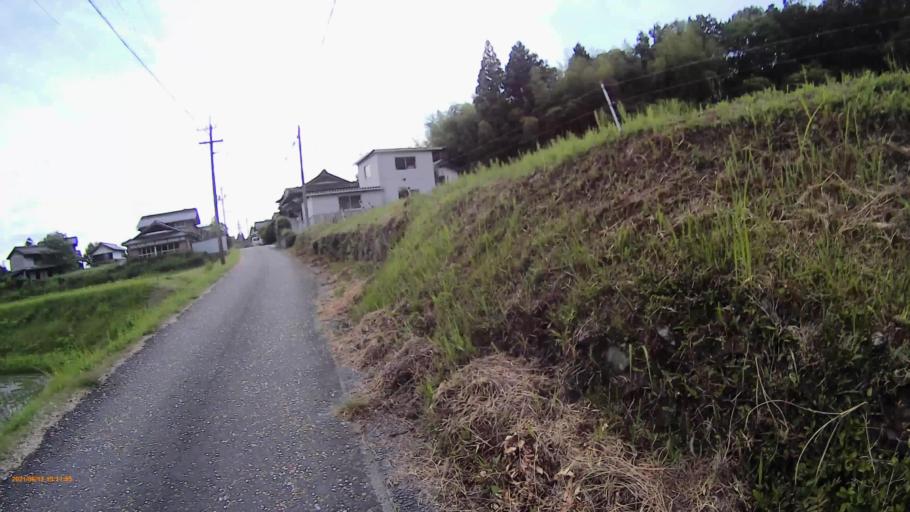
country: JP
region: Gifu
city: Mizunami
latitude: 35.4467
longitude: 137.3572
